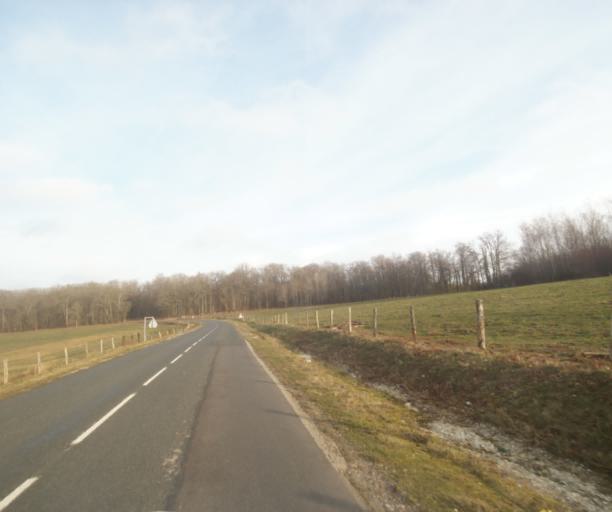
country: FR
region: Champagne-Ardenne
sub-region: Departement de la Marne
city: Sermaize-les-Bains
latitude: 48.7478
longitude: 4.9042
